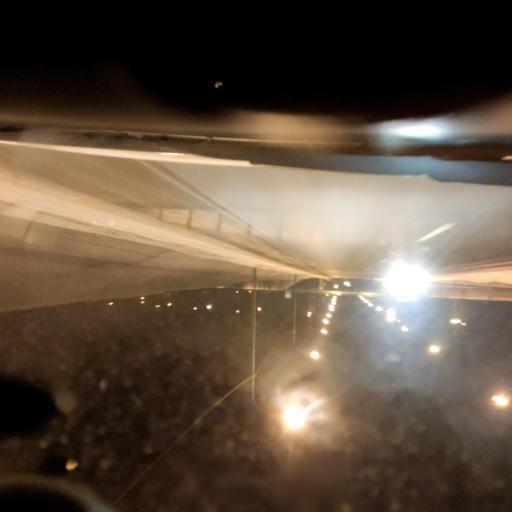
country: RU
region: Kursk
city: Fatezh
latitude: 52.0960
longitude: 35.8208
